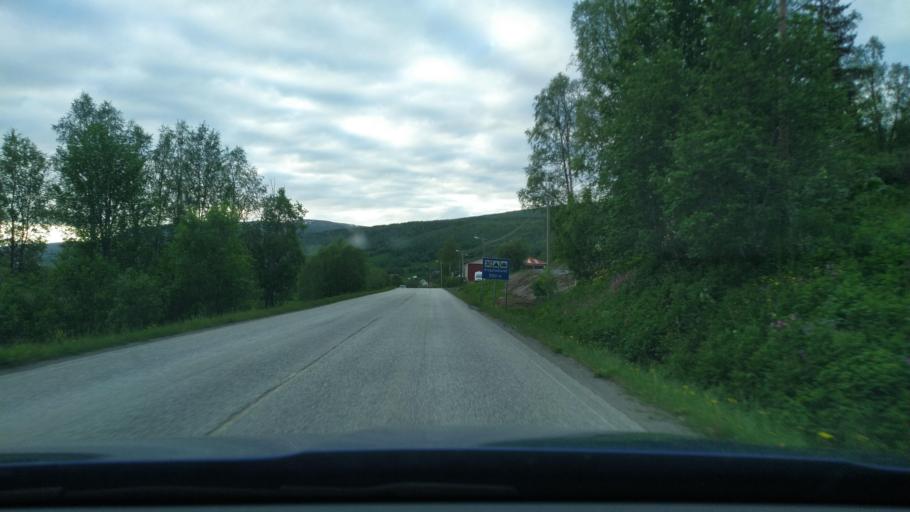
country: NO
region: Troms
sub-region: Sorreisa
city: Sorreisa
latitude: 69.1152
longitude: 18.2168
